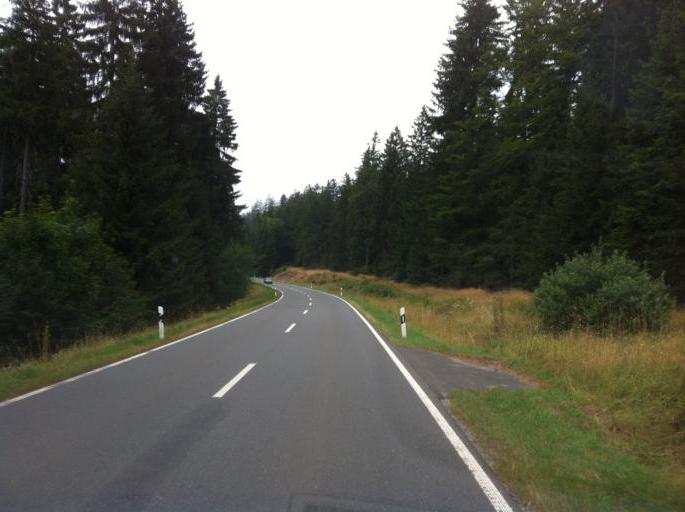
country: DE
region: Bavaria
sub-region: Upper Franconia
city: Bischofsgrun
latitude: 50.0719
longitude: 11.7732
